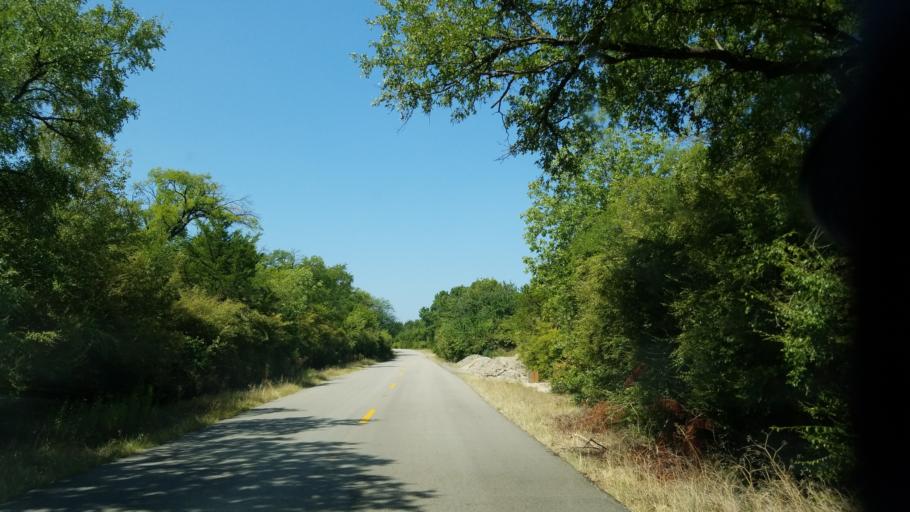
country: US
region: Texas
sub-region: Dallas County
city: Cockrell Hill
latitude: 32.7107
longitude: -96.9202
